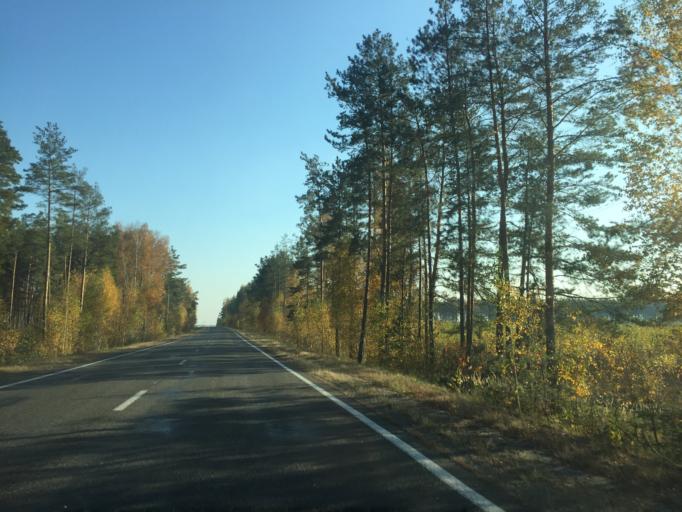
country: BY
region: Gomel
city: Dobrush
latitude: 52.3328
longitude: 31.2378
